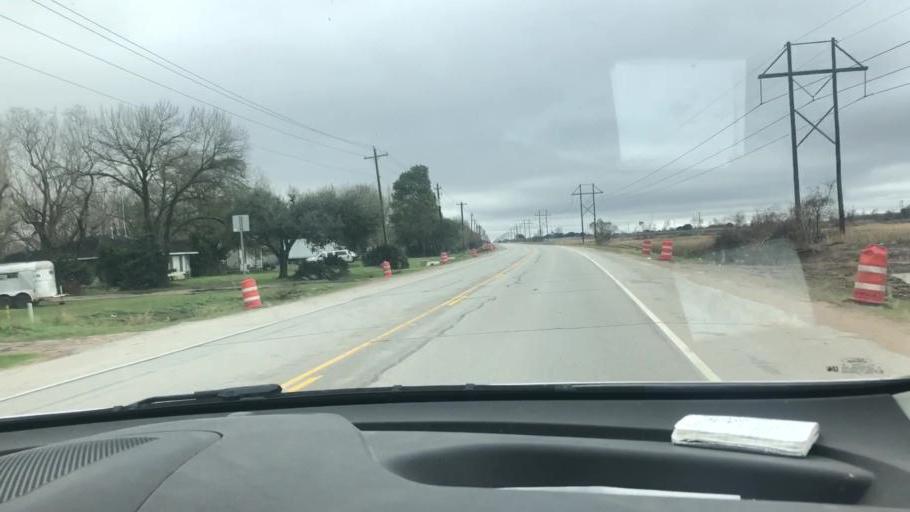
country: US
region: Texas
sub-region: Wharton County
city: Boling
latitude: 29.2125
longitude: -96.0271
